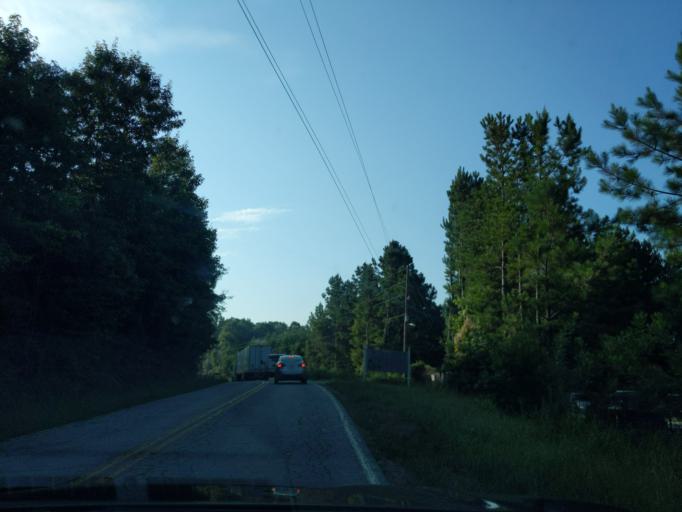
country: US
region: South Carolina
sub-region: Spartanburg County
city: Woodruff
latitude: 34.7879
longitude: -81.9714
